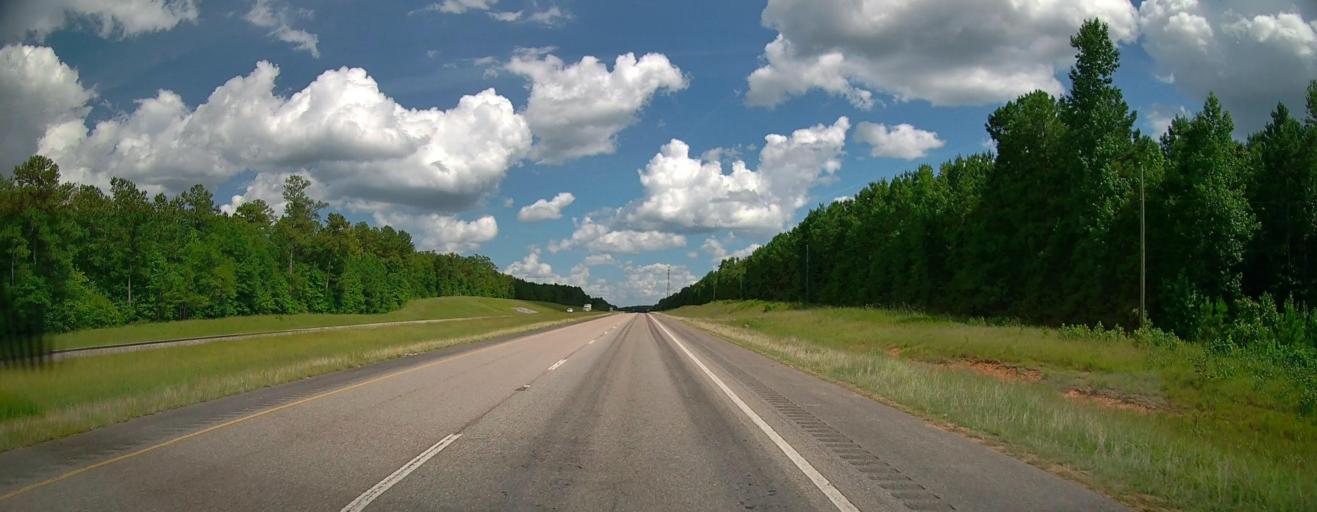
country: US
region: Mississippi
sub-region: Lowndes County
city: New Hope
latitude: 33.4573
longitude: -88.2209
